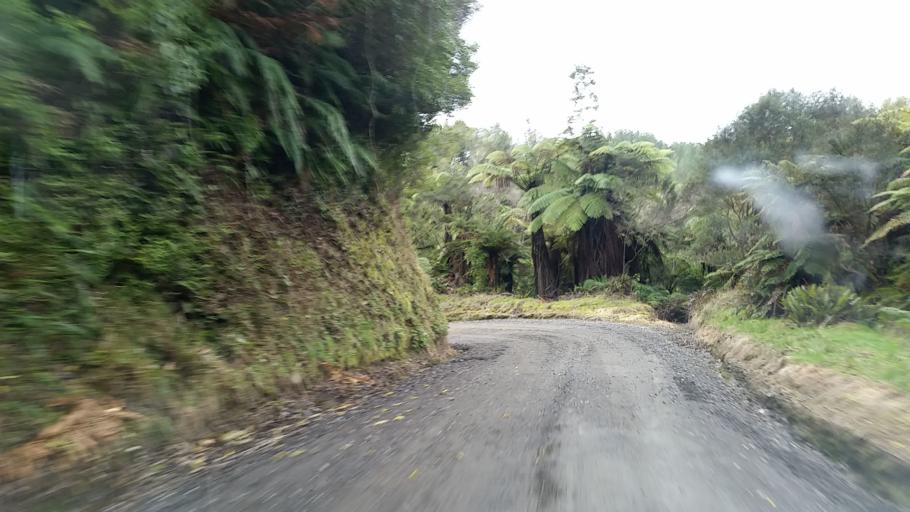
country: NZ
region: Taranaki
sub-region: New Plymouth District
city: Waitara
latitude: -39.1611
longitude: 174.5506
